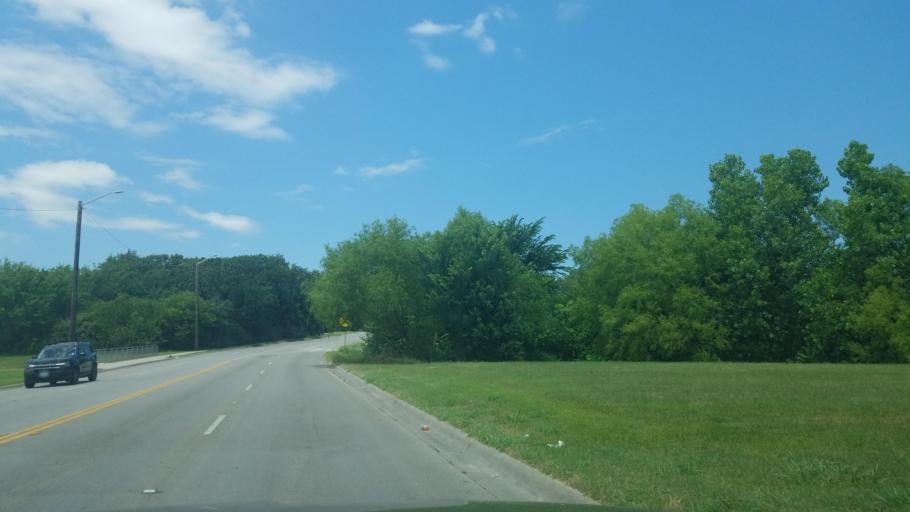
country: US
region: Texas
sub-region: Denton County
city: Denton
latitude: 33.2299
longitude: -97.1058
